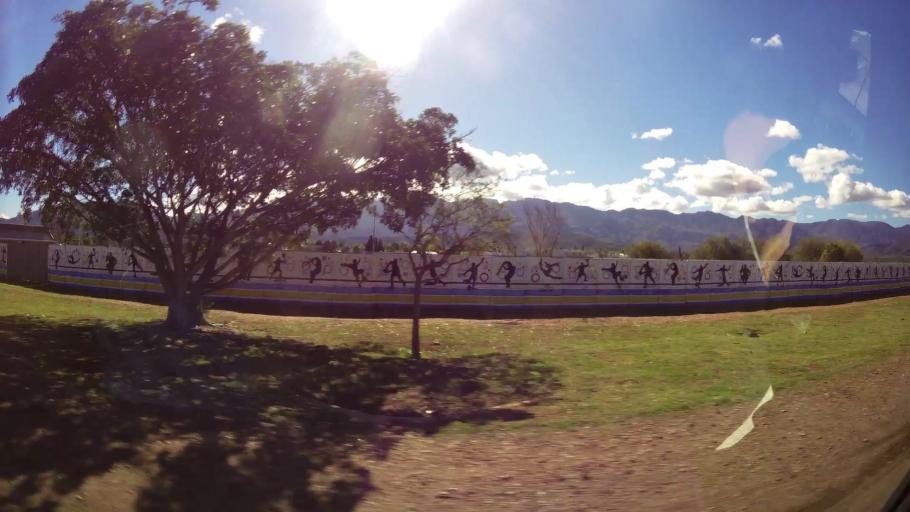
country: ZA
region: Western Cape
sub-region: Cape Winelands District Municipality
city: Ashton
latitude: -33.8137
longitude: 19.8962
